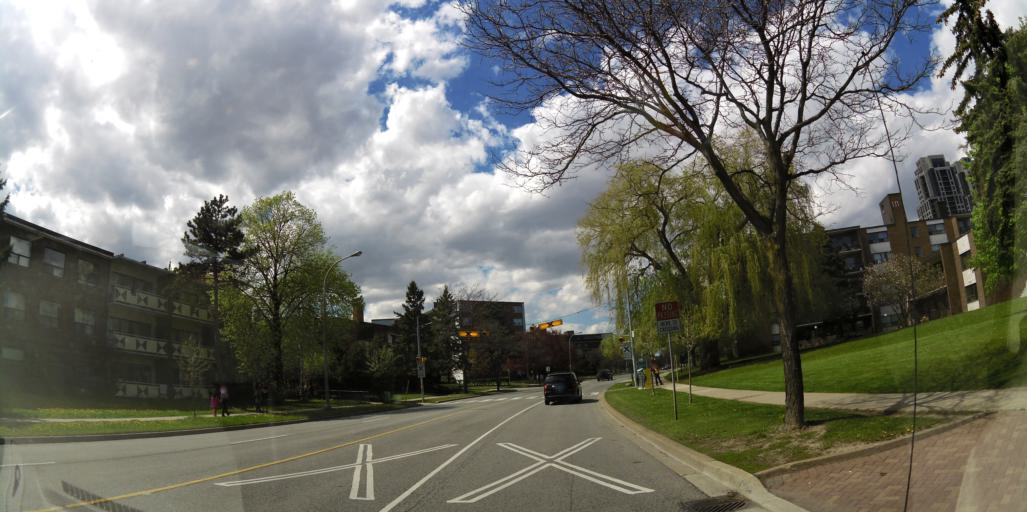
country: CA
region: Ontario
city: Etobicoke
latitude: 43.6376
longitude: -79.5638
